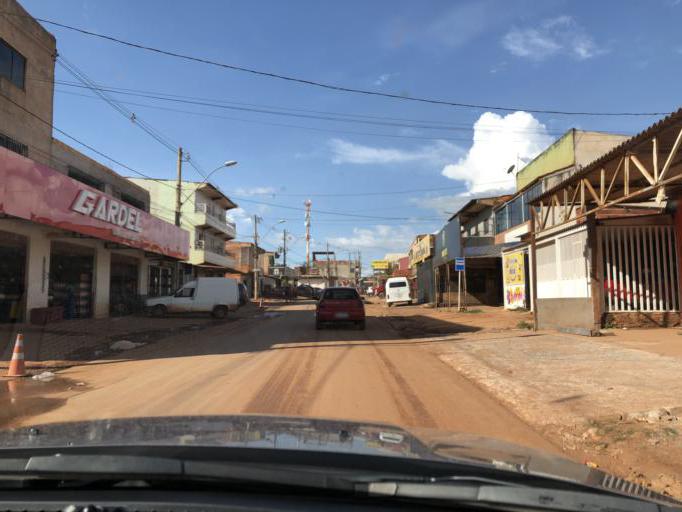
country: BR
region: Federal District
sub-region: Brasilia
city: Brasilia
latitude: -15.8192
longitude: -48.1542
